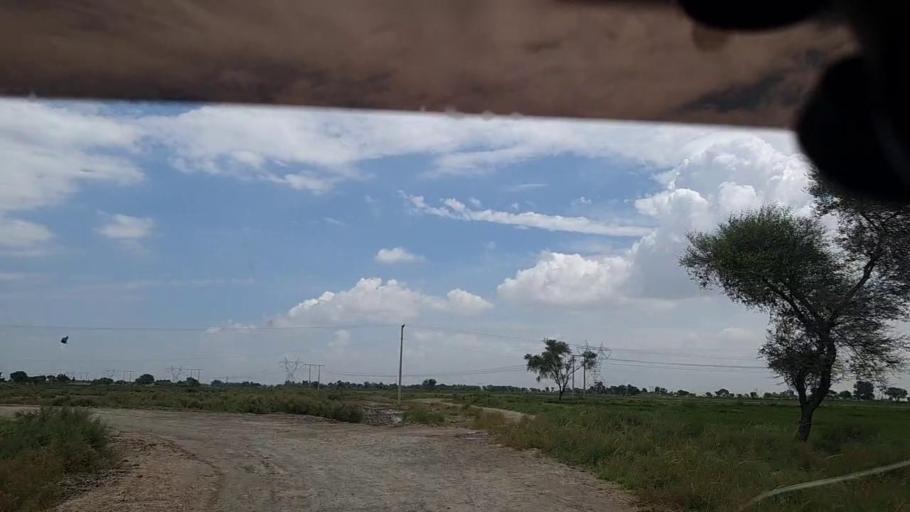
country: PK
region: Sindh
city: Ghauspur
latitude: 28.1144
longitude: 68.9877
